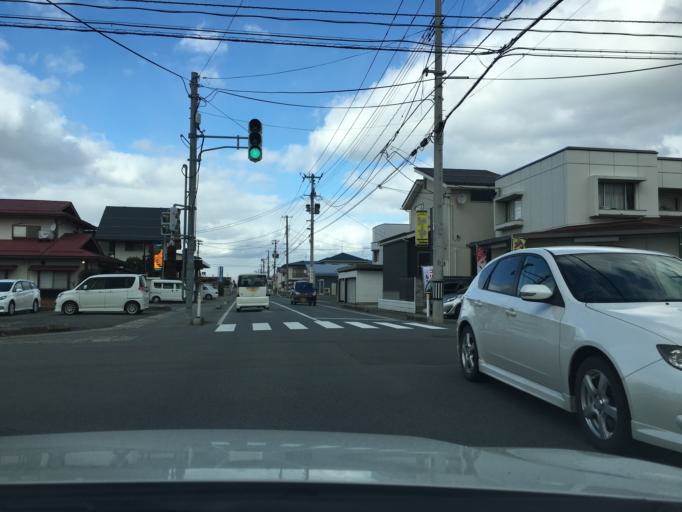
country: JP
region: Yamagata
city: Yamagata-shi
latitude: 38.2476
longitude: 140.3133
